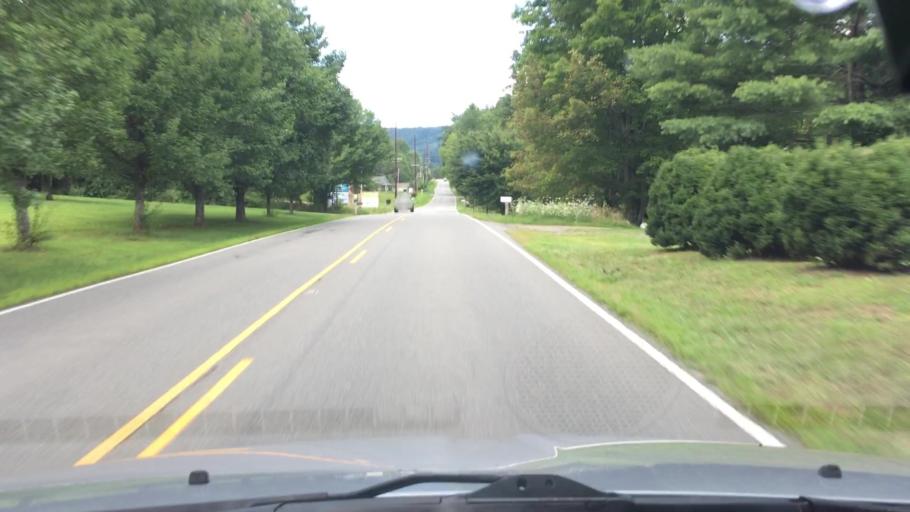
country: US
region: North Carolina
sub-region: Yancey County
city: Burnsville
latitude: 35.8452
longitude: -82.1918
